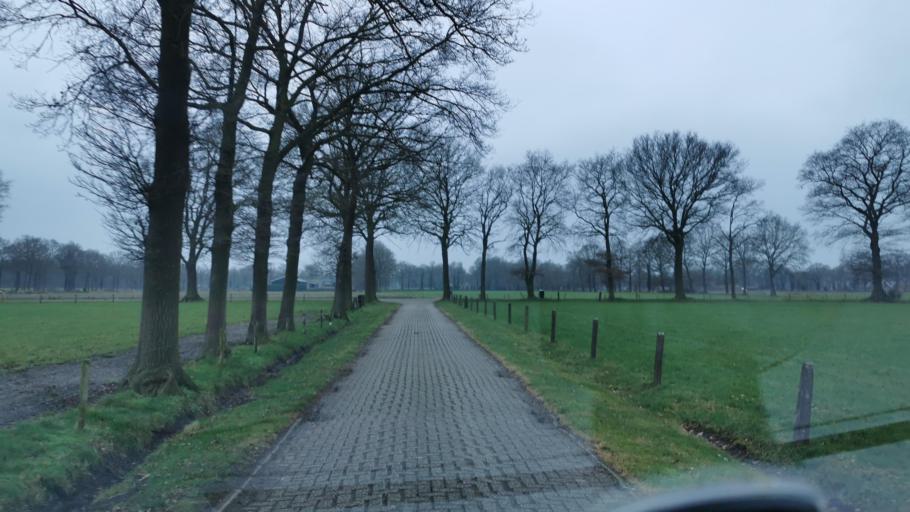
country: NL
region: Overijssel
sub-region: Gemeente Borne
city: Borne
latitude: 52.3427
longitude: 6.7906
